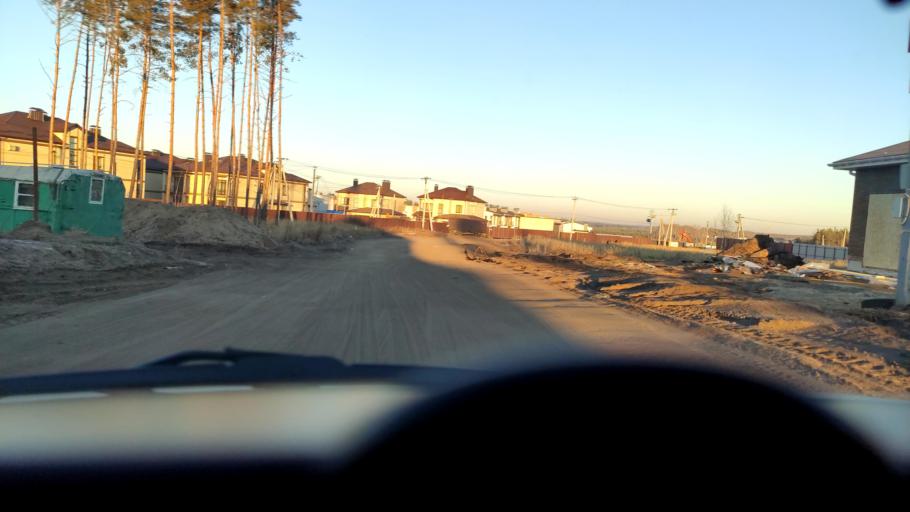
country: RU
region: Voronezj
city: Podgornoye
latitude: 51.7464
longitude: 39.1423
